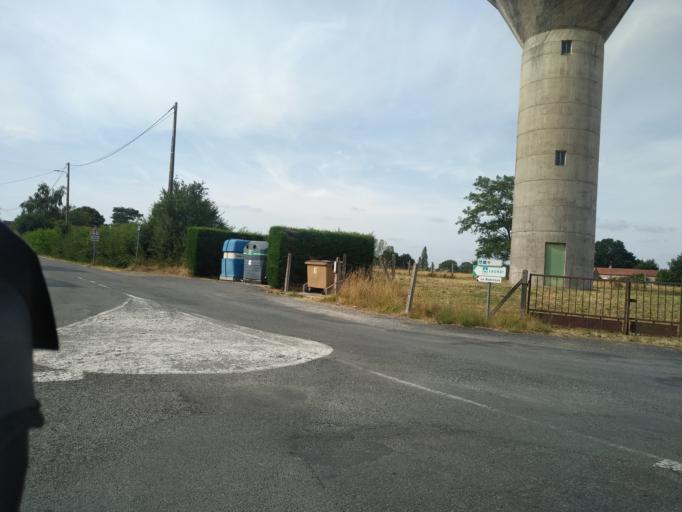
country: FR
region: Bourgogne
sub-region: Departement de Saone-et-Loire
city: Bourbon-Lancy
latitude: 46.6293
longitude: 3.7572
